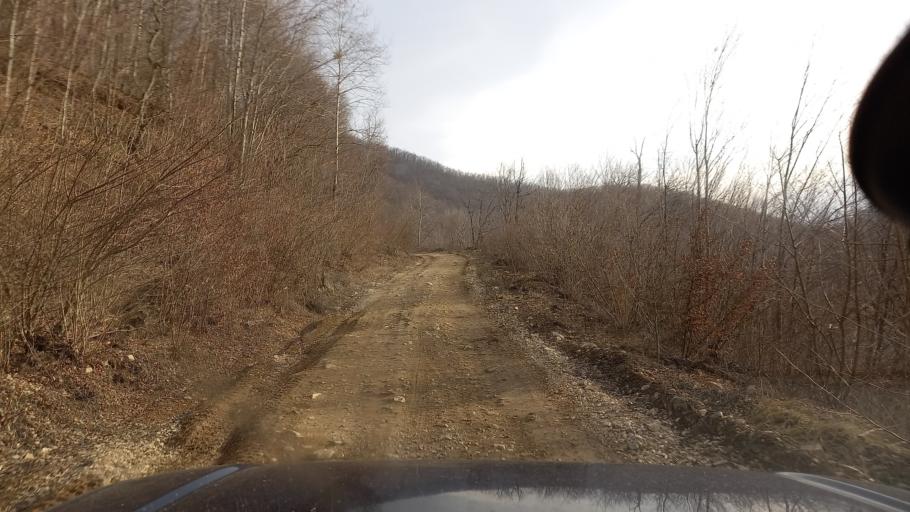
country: RU
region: Adygeya
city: Kamennomostskiy
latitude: 44.1488
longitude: 40.3020
